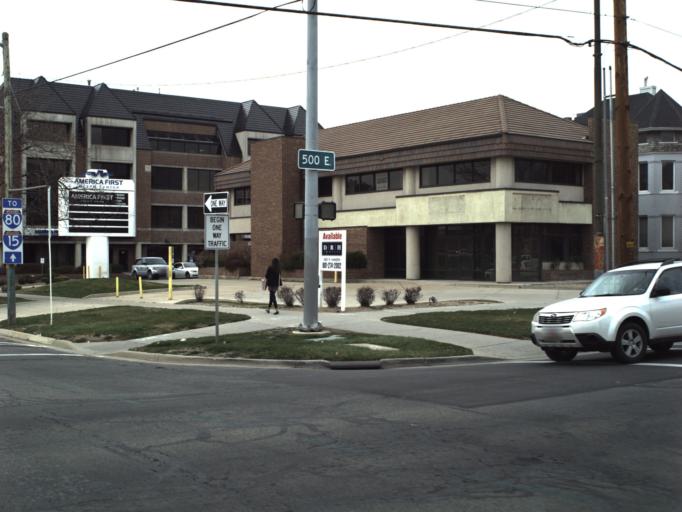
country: US
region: Utah
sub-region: Salt Lake County
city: Salt Lake City
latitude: 40.7585
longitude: -111.8768
